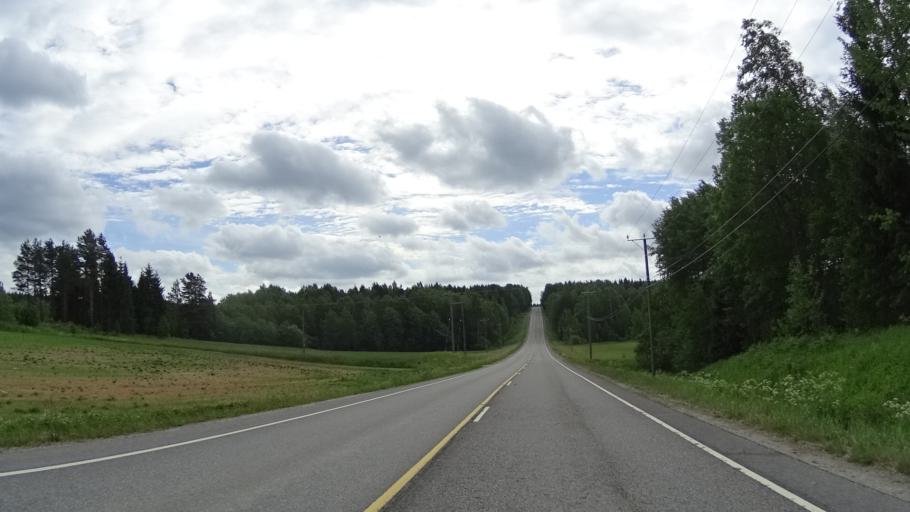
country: FI
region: Uusimaa
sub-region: Helsinki
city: Vihti
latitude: 60.2972
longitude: 24.3835
